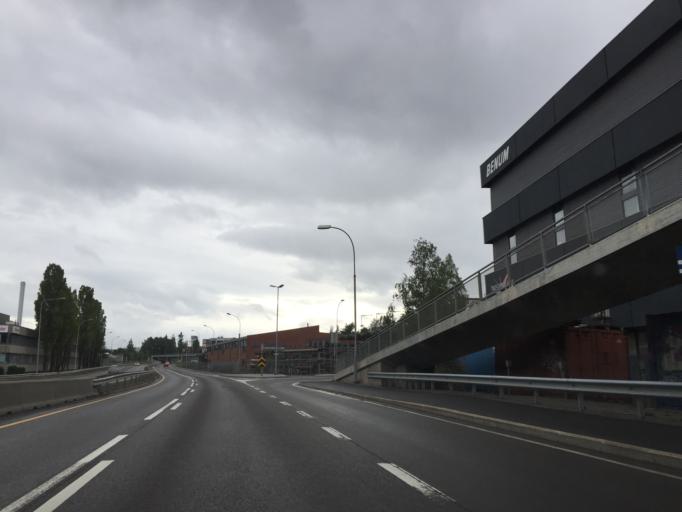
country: NO
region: Oslo
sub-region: Oslo
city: Oslo
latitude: 59.9365
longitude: 10.8337
